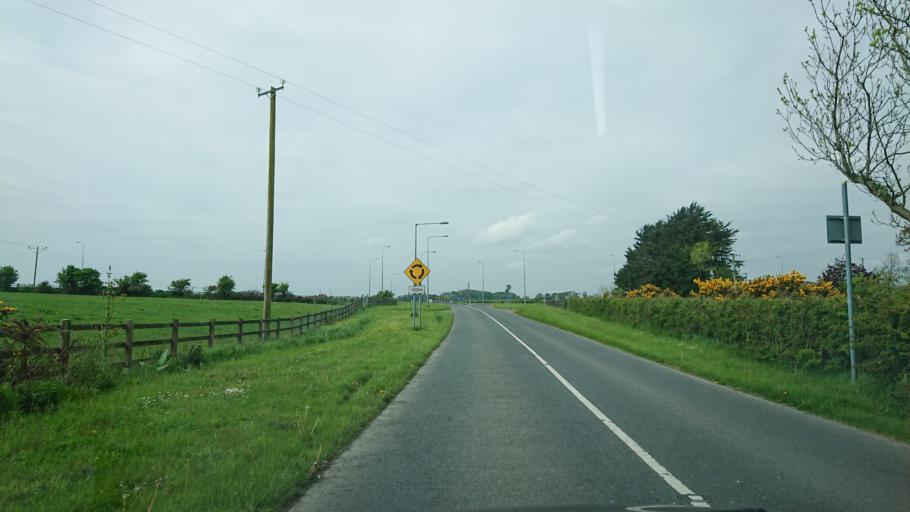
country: IE
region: Munster
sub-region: Waterford
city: Waterford
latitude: 52.2097
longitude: -7.0862
